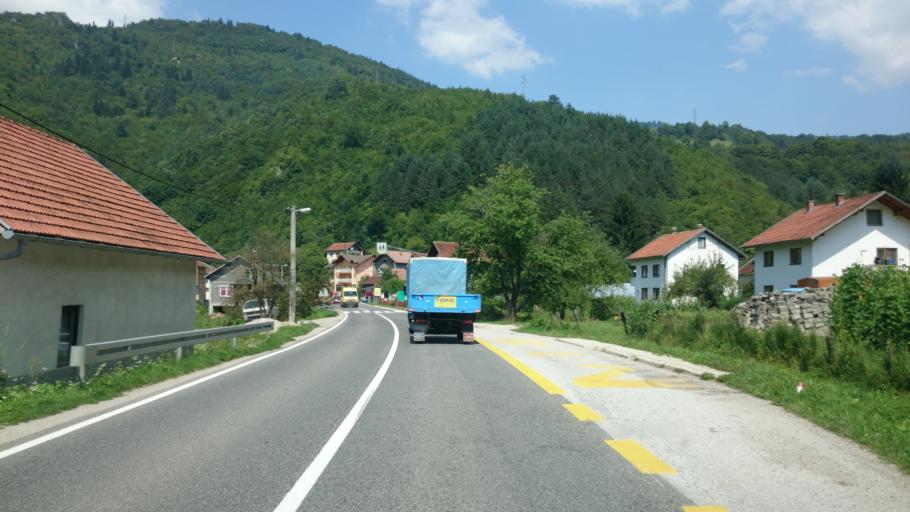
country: BA
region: Federation of Bosnia and Herzegovina
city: Jajce
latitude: 44.2291
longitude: 17.3143
